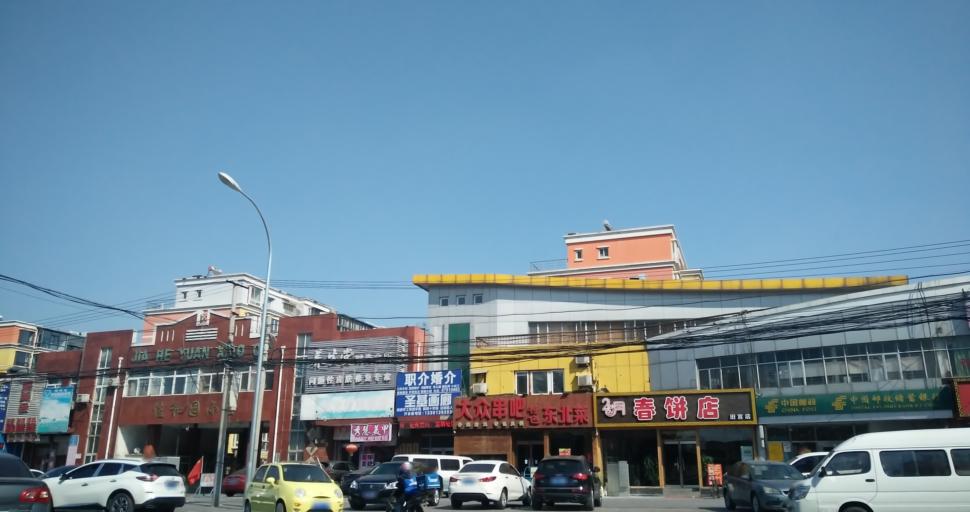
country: CN
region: Beijing
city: Jiugong
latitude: 39.8045
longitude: 116.4377
